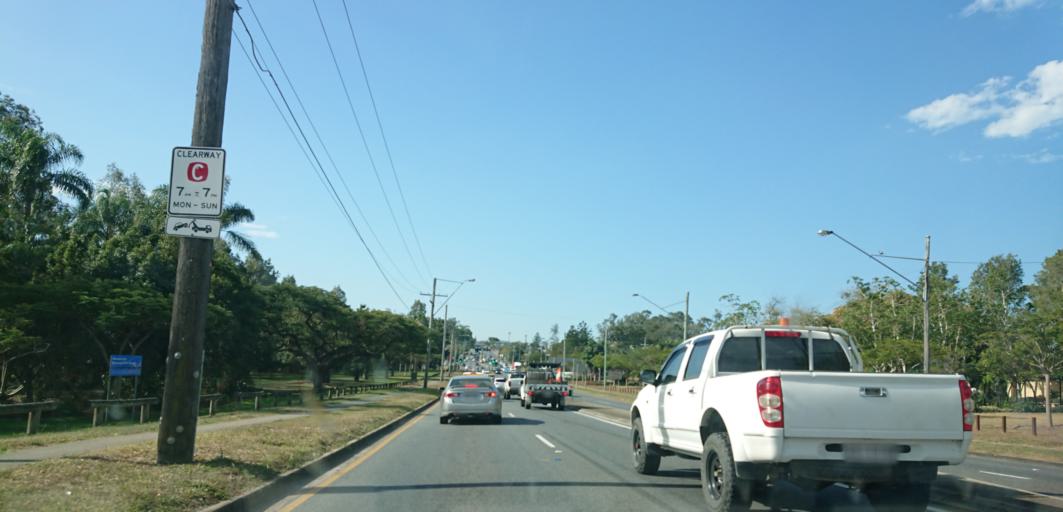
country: AU
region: Queensland
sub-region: Brisbane
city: Yeerongpilly
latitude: -27.5265
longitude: 153.0215
